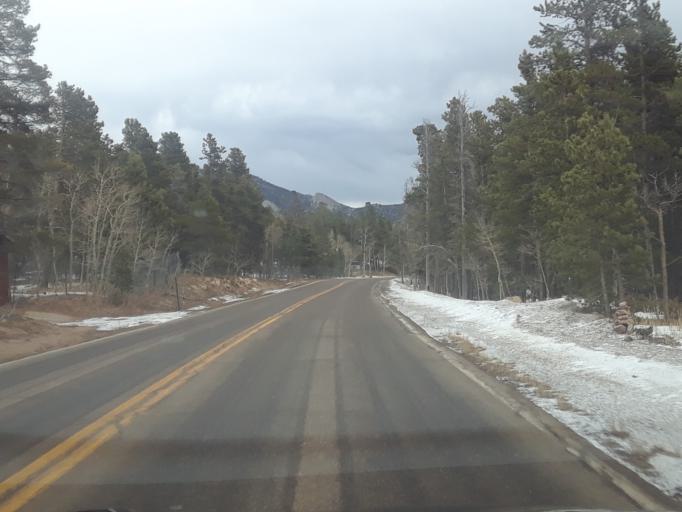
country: US
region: Colorado
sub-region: Gilpin County
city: Central City
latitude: 39.8398
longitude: -105.4741
